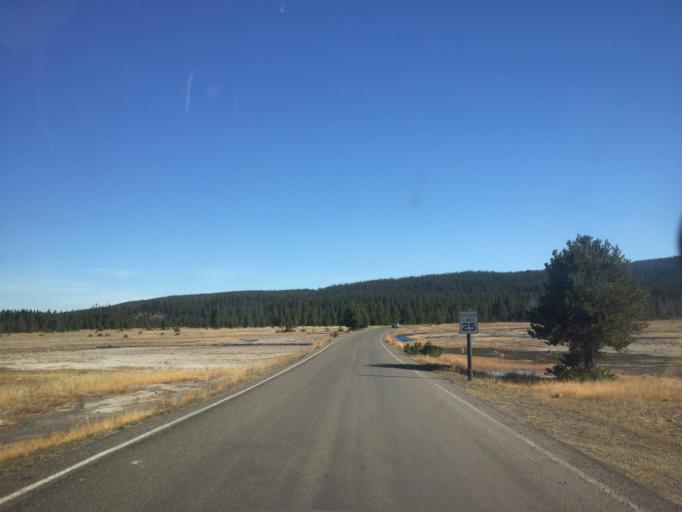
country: US
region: Montana
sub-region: Gallatin County
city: West Yellowstone
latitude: 44.5397
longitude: -110.8022
